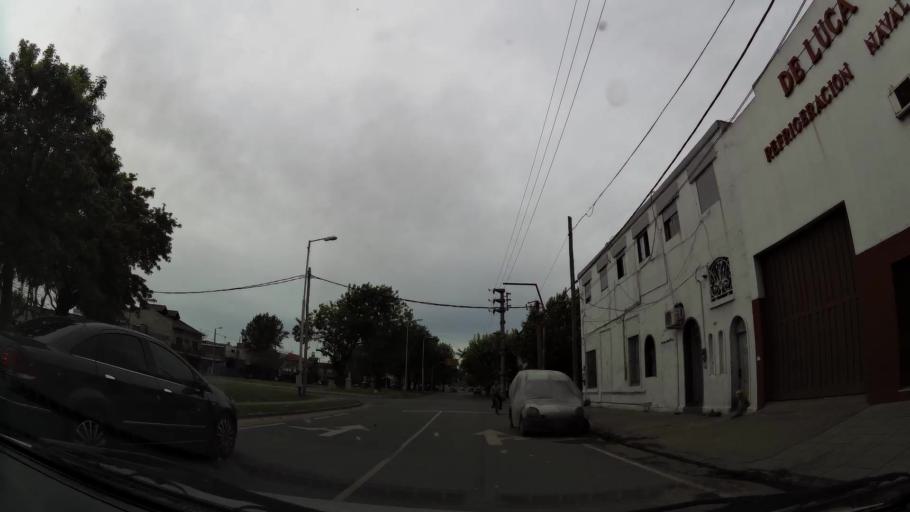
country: AR
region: Buenos Aires
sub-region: Partido de Avellaneda
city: Avellaneda
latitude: -34.6569
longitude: -58.3602
